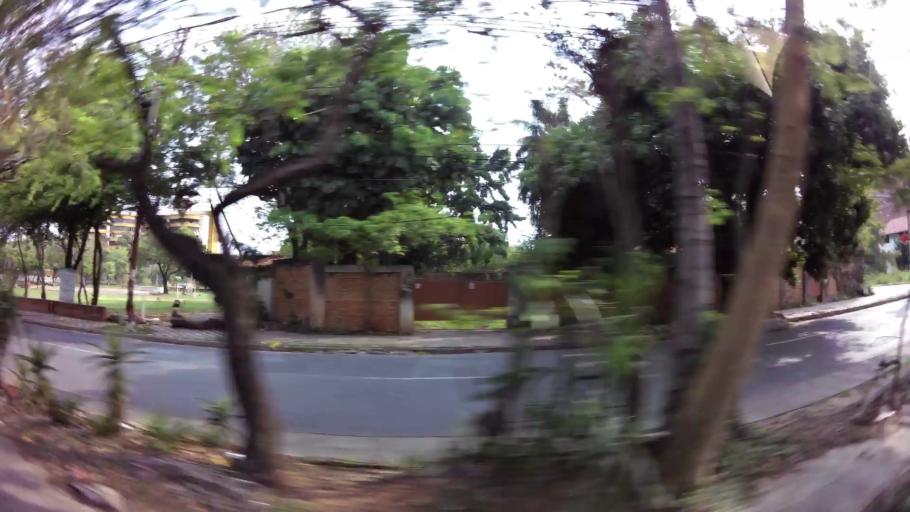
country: PY
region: Asuncion
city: Asuncion
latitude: -25.2771
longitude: -57.5648
